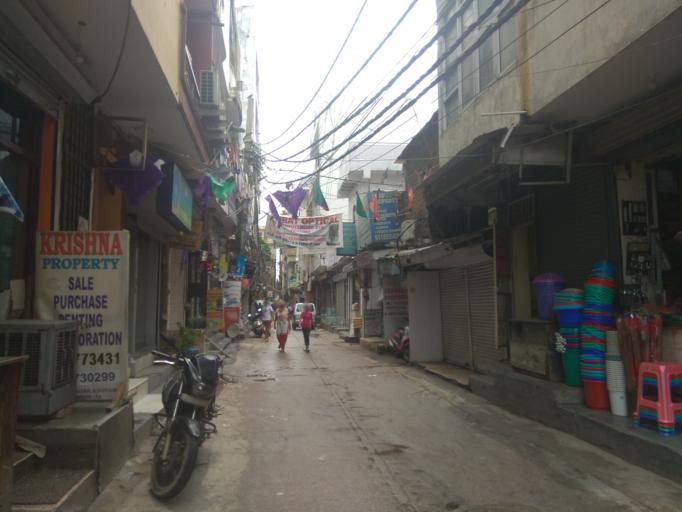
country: IN
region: NCT
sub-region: New Delhi
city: New Delhi
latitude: 28.5743
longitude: 77.2568
